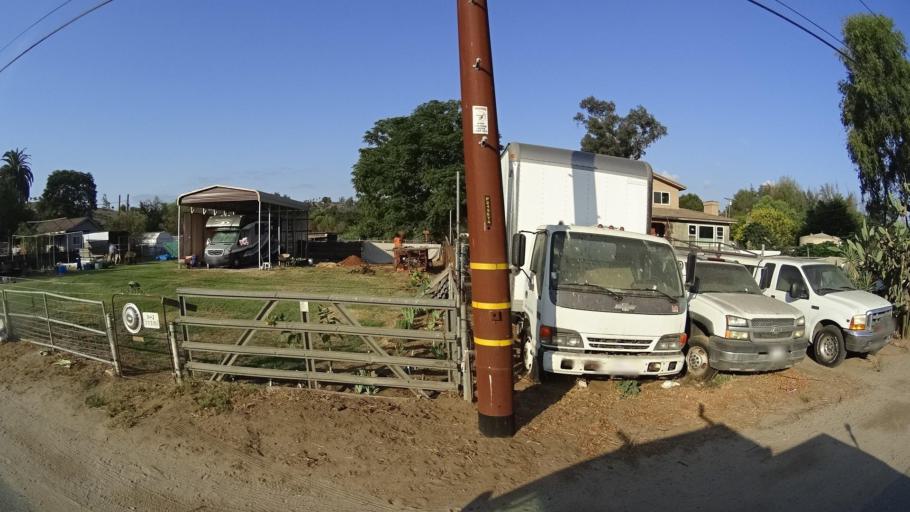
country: US
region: California
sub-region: San Diego County
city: Eucalyptus Hills
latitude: 32.8918
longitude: -116.9273
